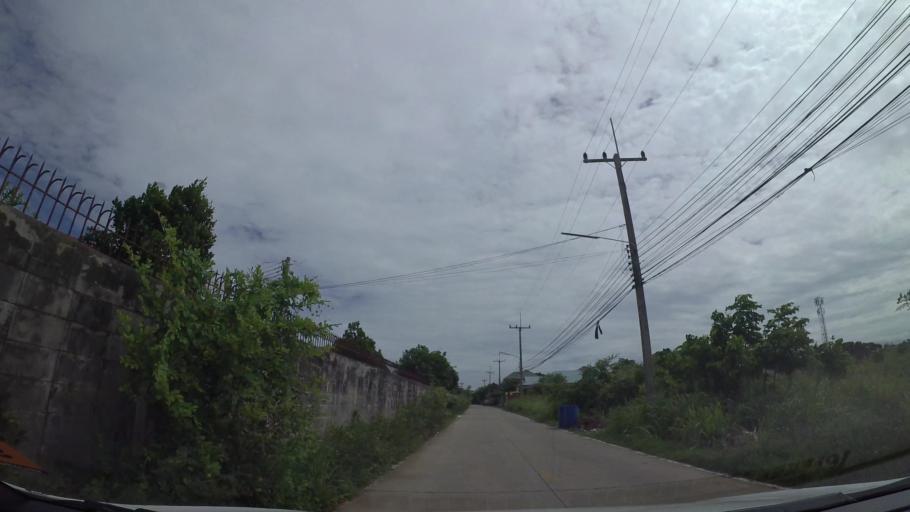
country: TH
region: Rayong
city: Rayong
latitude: 12.6640
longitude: 101.2845
